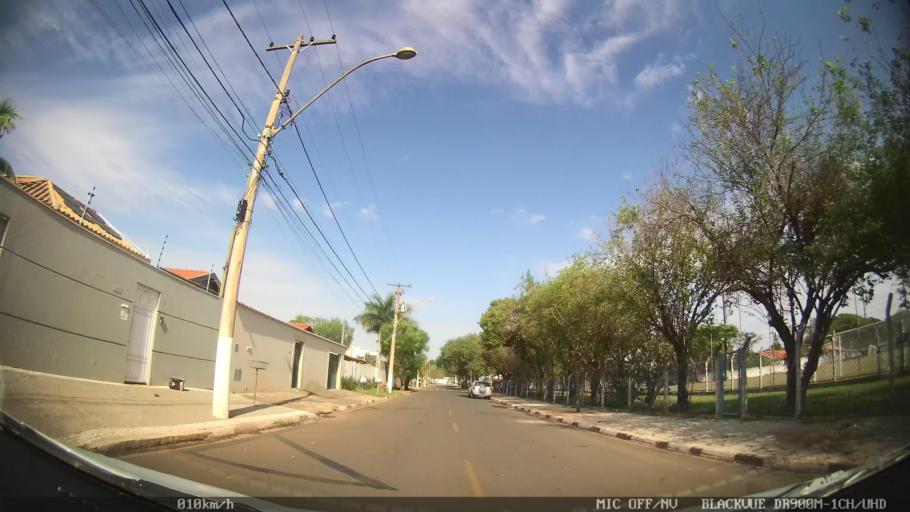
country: BR
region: Sao Paulo
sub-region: Paulinia
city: Paulinia
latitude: -22.7800
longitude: -47.1371
